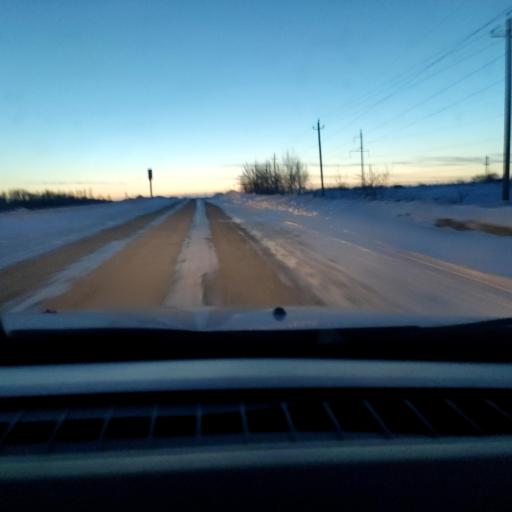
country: RU
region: Samara
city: Georgiyevka
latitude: 53.3326
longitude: 50.8955
